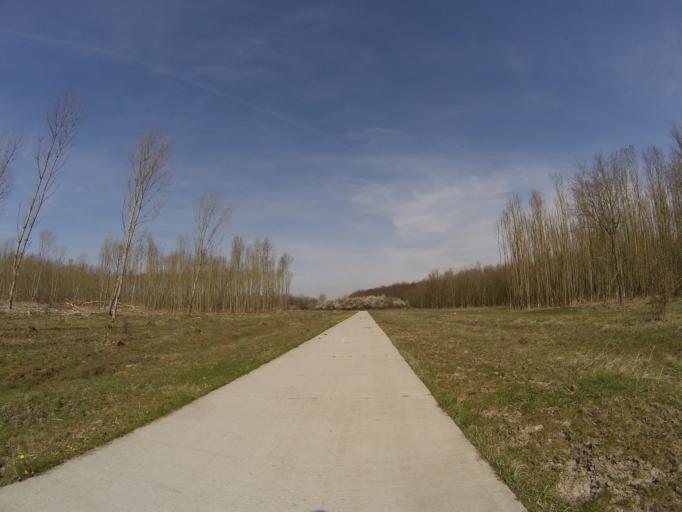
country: NL
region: Flevoland
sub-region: Gemeente Zeewolde
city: Zeewolde
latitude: 52.3073
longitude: 5.4595
